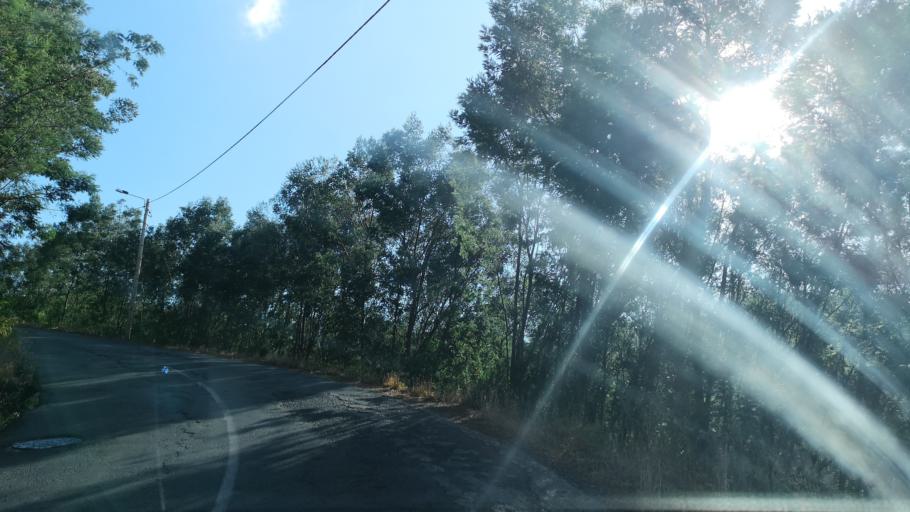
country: PT
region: Madeira
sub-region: Santa Cruz
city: Camacha
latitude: 32.6691
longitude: -16.8383
